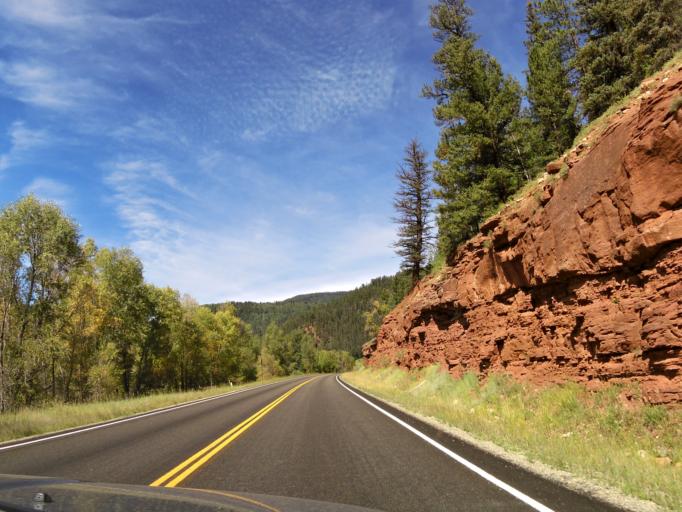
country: US
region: Colorado
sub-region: Montezuma County
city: Mancos
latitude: 37.5922
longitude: -108.1273
